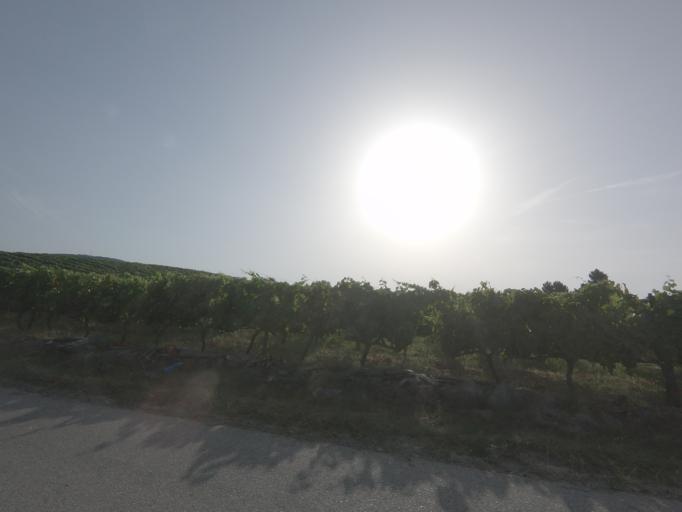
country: PT
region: Vila Real
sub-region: Sabrosa
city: Sabrosa
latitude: 41.2369
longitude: -7.4701
